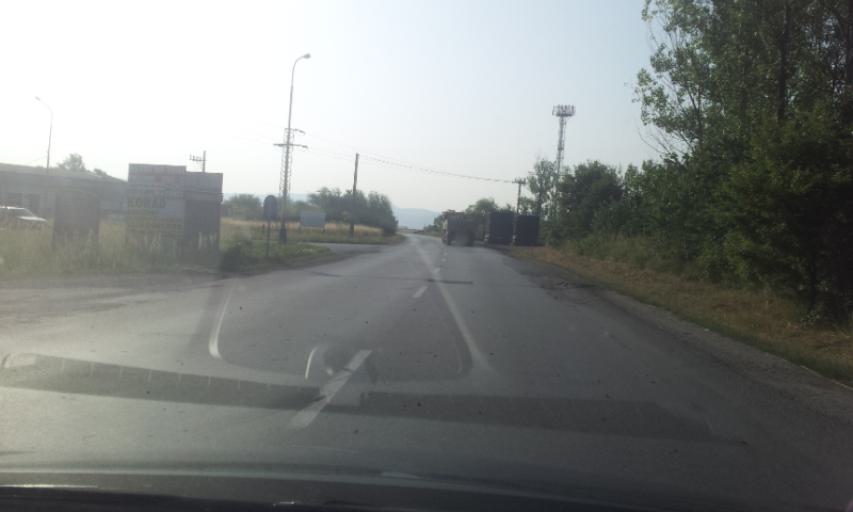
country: SK
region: Kosicky
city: Kosice
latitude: 48.6183
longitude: 21.2327
